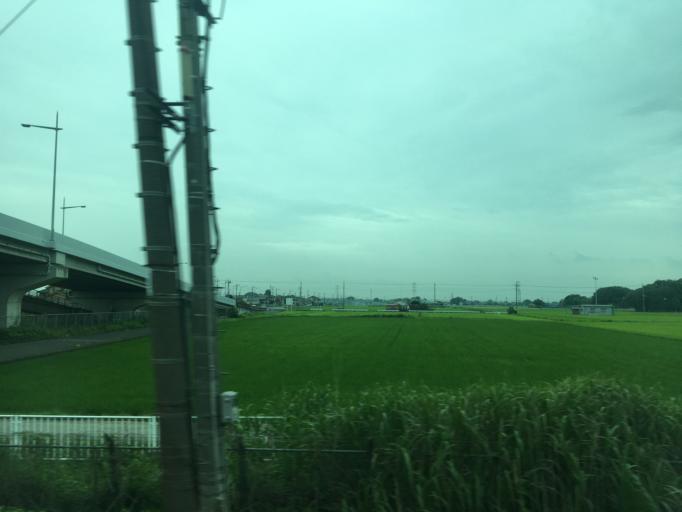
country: JP
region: Saitama
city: Kurihashi
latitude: 36.1189
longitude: 139.6861
